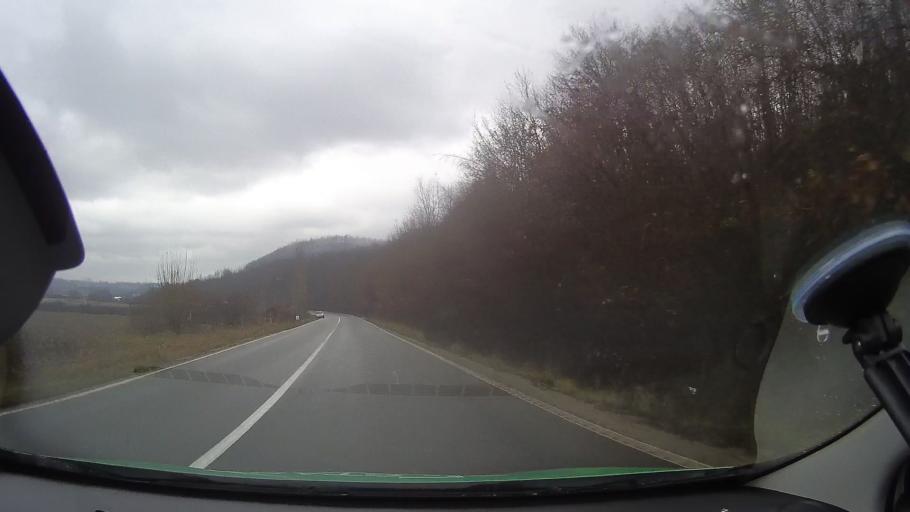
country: RO
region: Arad
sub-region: Comuna Almas
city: Almas
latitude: 46.2975
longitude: 22.2034
